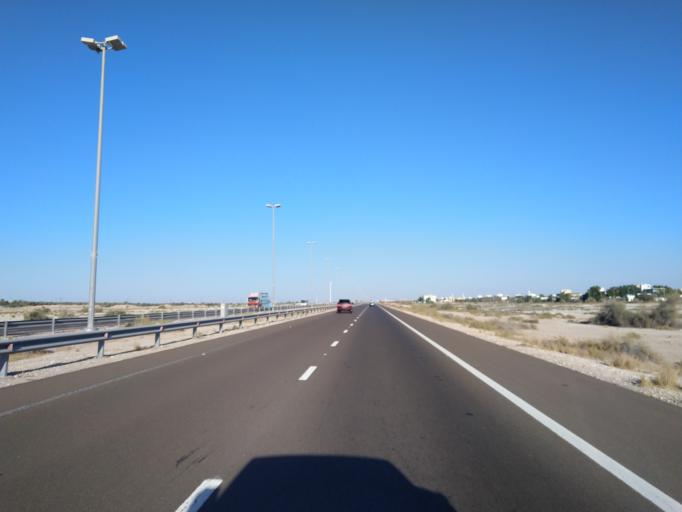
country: OM
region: Al Buraimi
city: Al Buraymi
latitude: 24.5214
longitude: 55.5286
